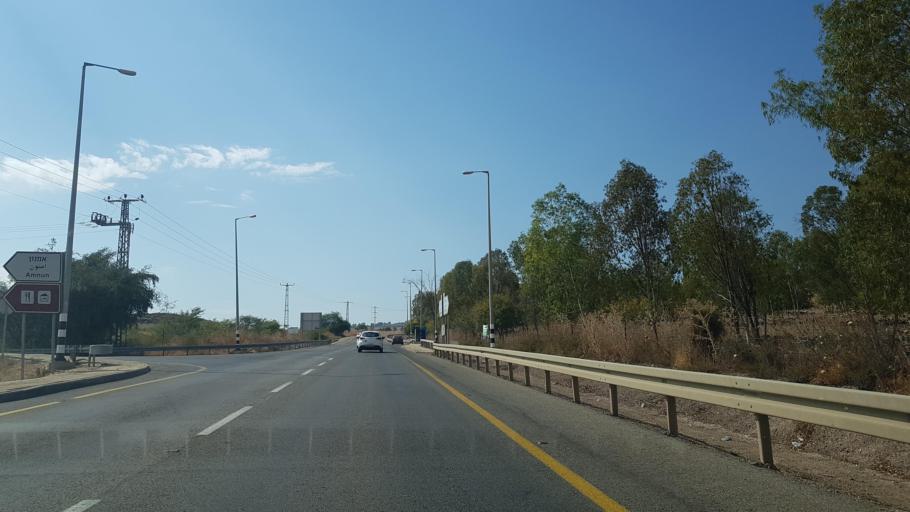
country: SY
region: Quneitra
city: Al Butayhah
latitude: 32.9104
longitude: 35.5797
